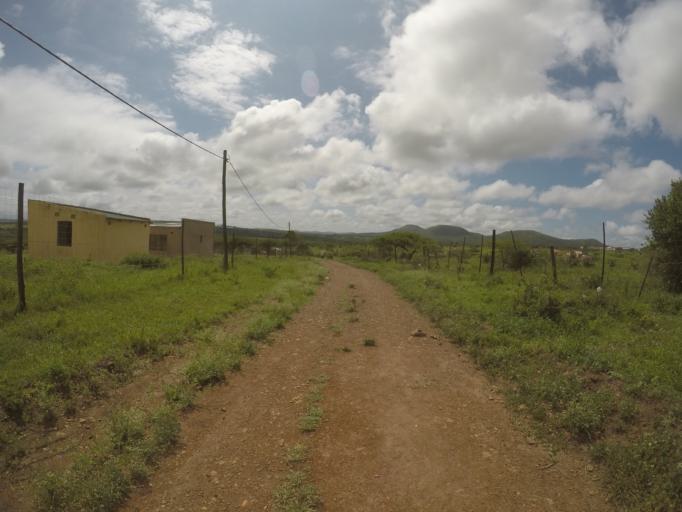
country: ZA
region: KwaZulu-Natal
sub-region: uThungulu District Municipality
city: Empangeni
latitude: -28.5730
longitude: 31.8405
